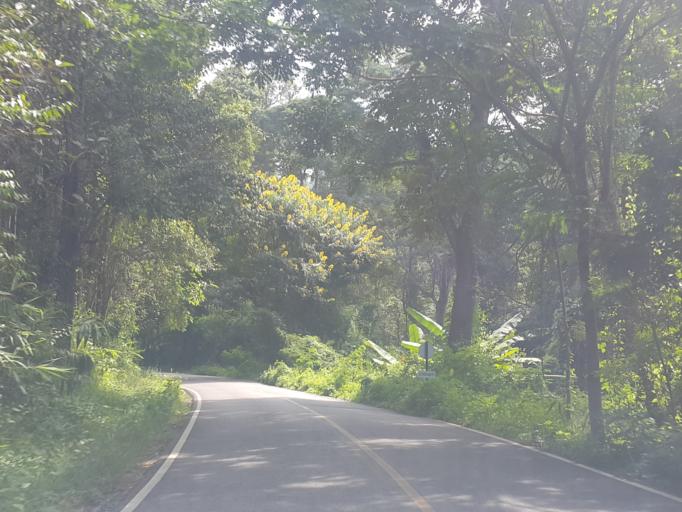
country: TH
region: Chiang Mai
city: Mae On
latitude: 18.8635
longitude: 99.2939
